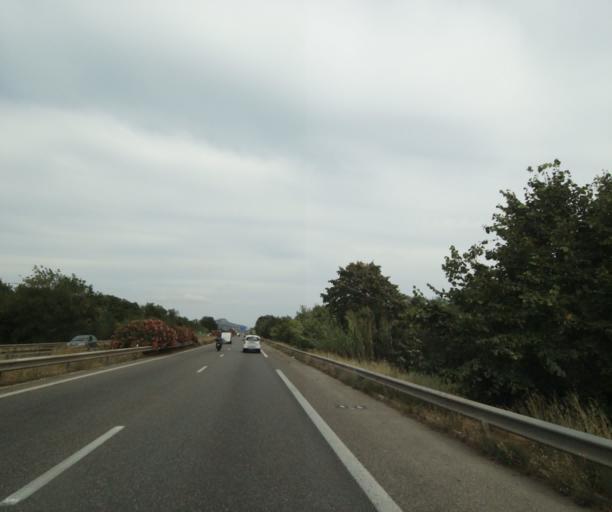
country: FR
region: Provence-Alpes-Cote d'Azur
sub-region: Departement du Var
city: La Crau
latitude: 43.1262
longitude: 6.0820
